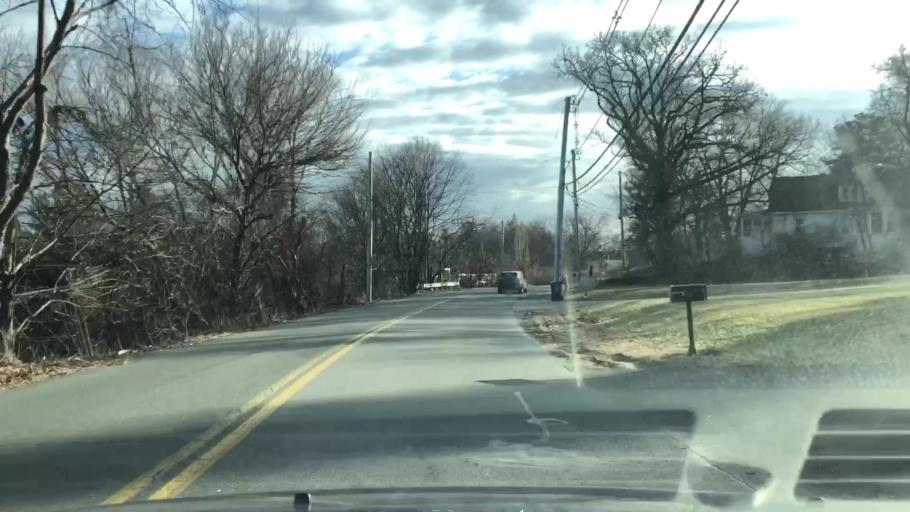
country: US
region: Massachusetts
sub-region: Middlesex County
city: Dracut
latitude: 42.6691
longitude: -71.3451
